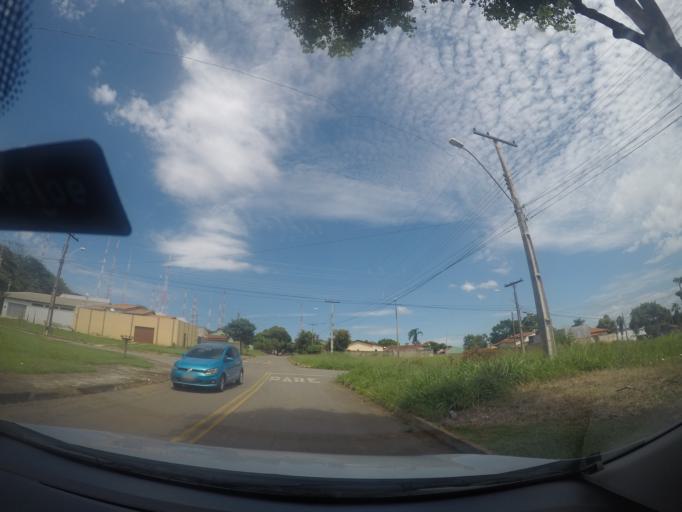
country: BR
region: Goias
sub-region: Goiania
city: Goiania
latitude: -16.6616
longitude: -49.3381
